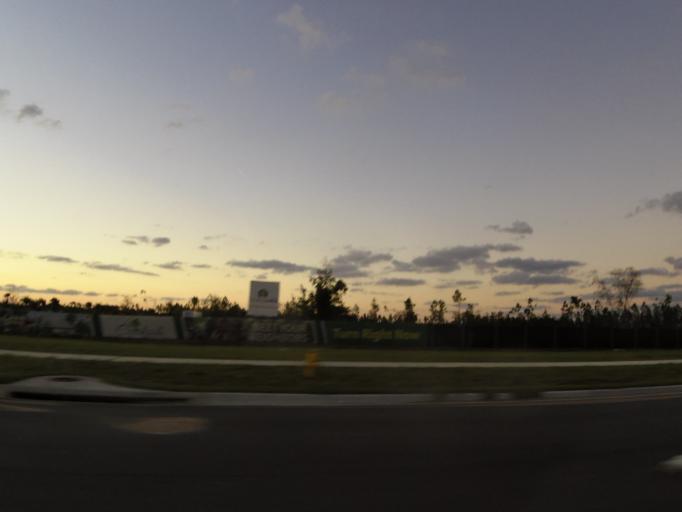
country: US
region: Florida
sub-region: Saint Johns County
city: Palm Valley
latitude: 30.0852
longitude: -81.4714
